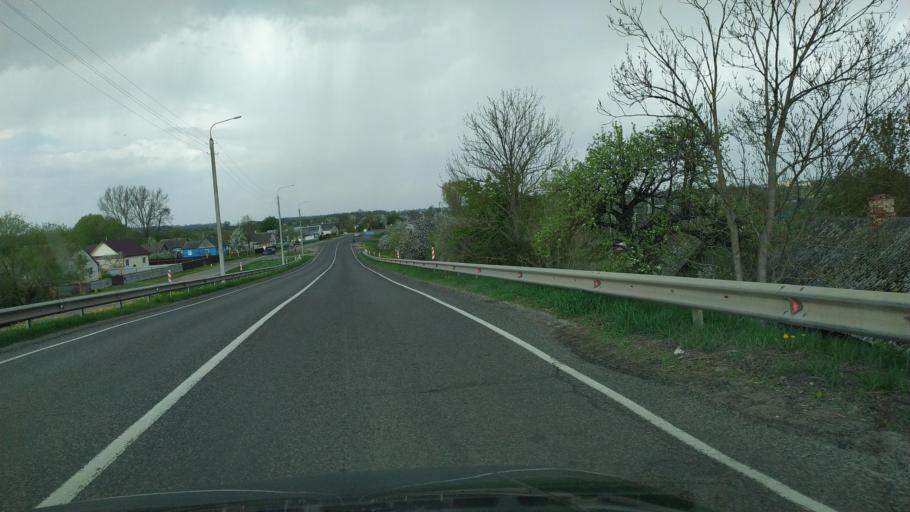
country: BY
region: Brest
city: Pruzhany
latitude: 52.4697
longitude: 24.5145
